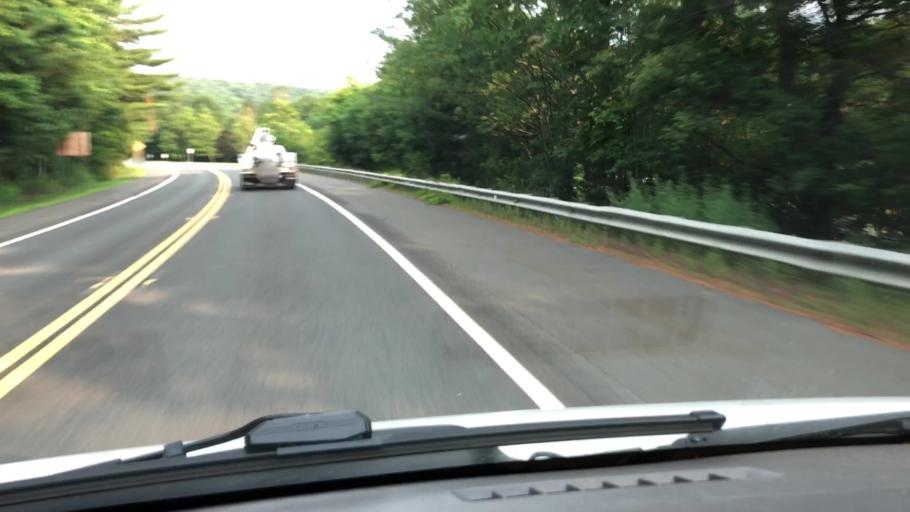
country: US
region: Massachusetts
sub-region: Berkshire County
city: Hinsdale
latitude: 42.4909
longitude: -72.9705
